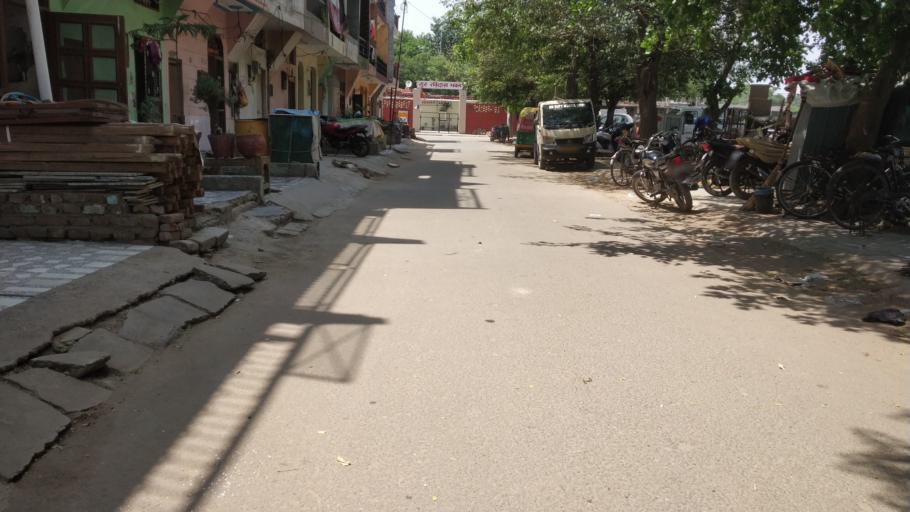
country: IN
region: Punjab
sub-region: Ajitgarh
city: Mohali
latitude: 30.7123
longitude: 76.7332
